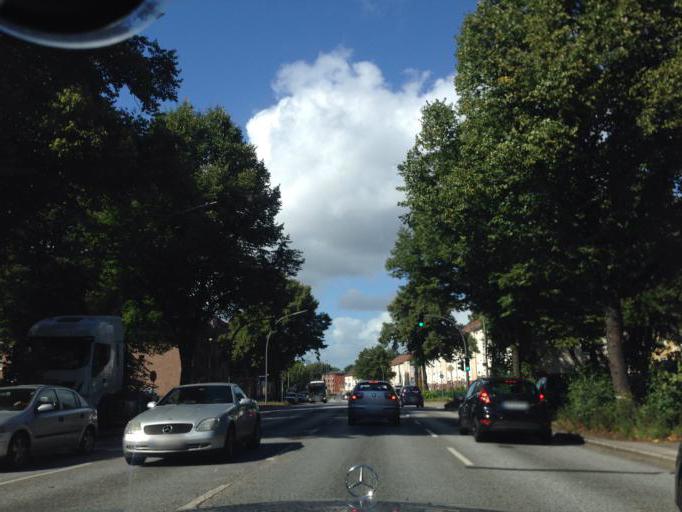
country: DE
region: Hamburg
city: Marienthal
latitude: 53.5846
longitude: 10.0664
